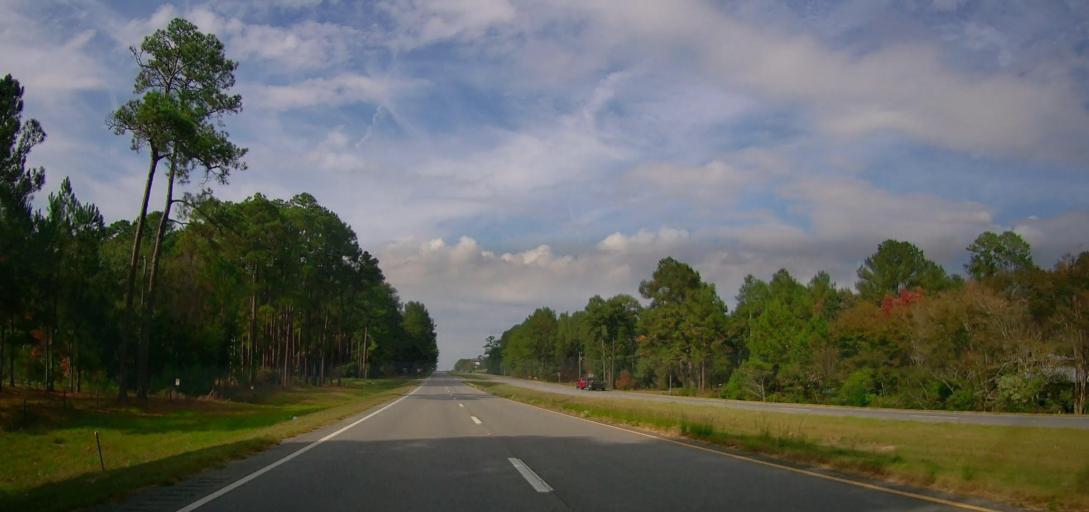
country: US
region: Georgia
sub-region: Thomas County
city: Meigs
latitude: 30.9687
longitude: -84.0333
